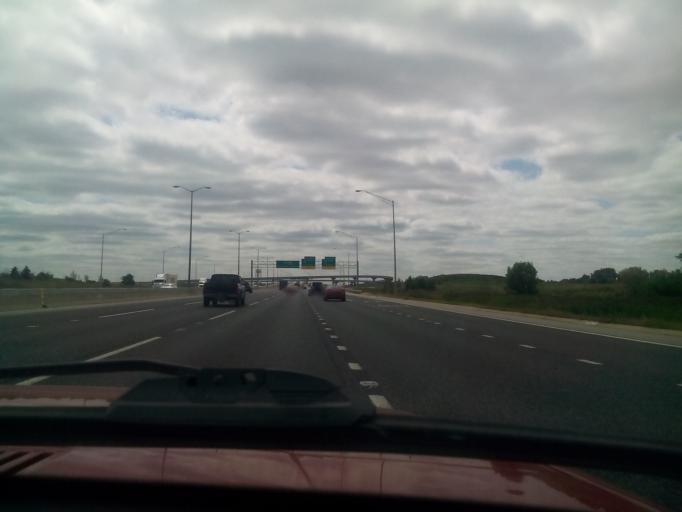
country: US
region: Illinois
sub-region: DuPage County
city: Woodridge
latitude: 41.7157
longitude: -88.0332
